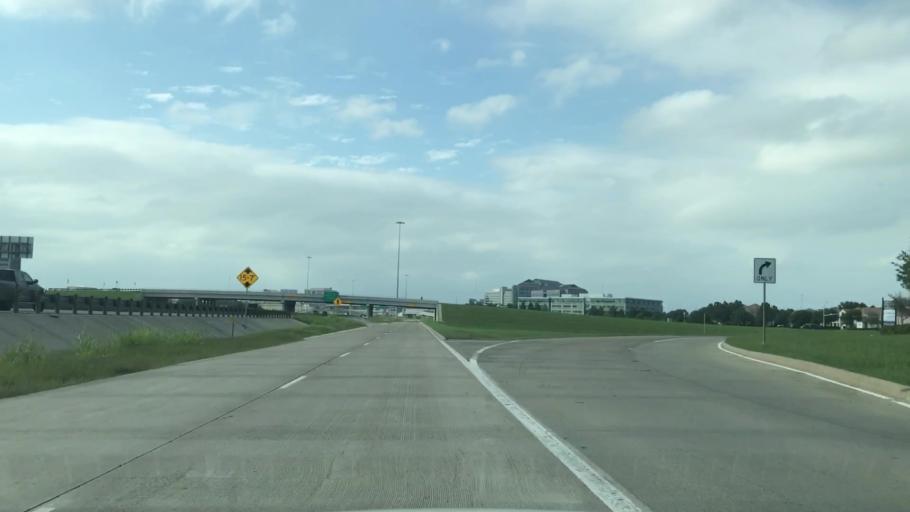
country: US
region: Texas
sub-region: Dallas County
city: Farmers Branch
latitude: 32.8891
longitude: -96.9595
